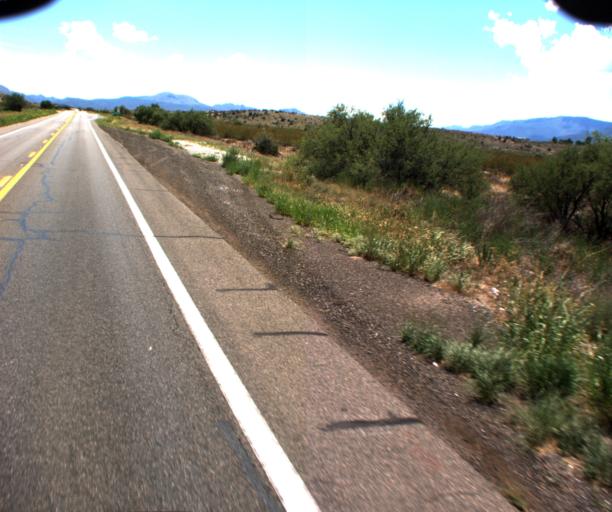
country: US
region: Arizona
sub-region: Yavapai County
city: Camp Verde
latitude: 34.5430
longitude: -111.8264
